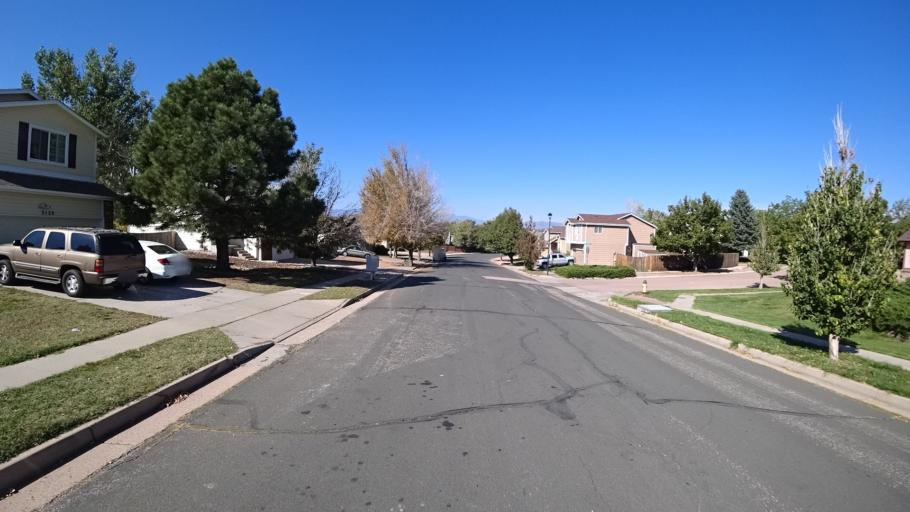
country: US
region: Colorado
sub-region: El Paso County
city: Cimarron Hills
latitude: 38.8770
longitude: -104.7054
